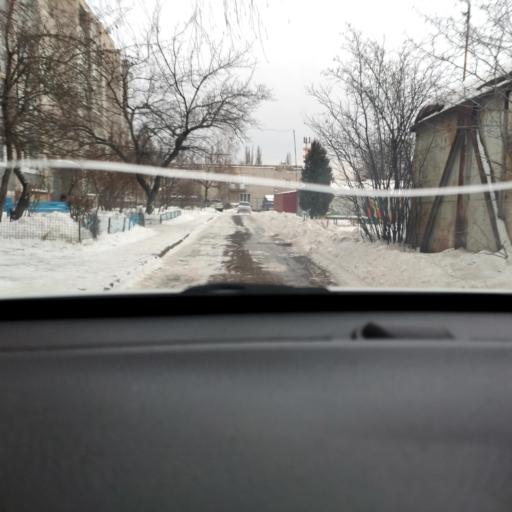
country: RU
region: Voronezj
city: Somovo
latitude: 51.7458
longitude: 39.3582
